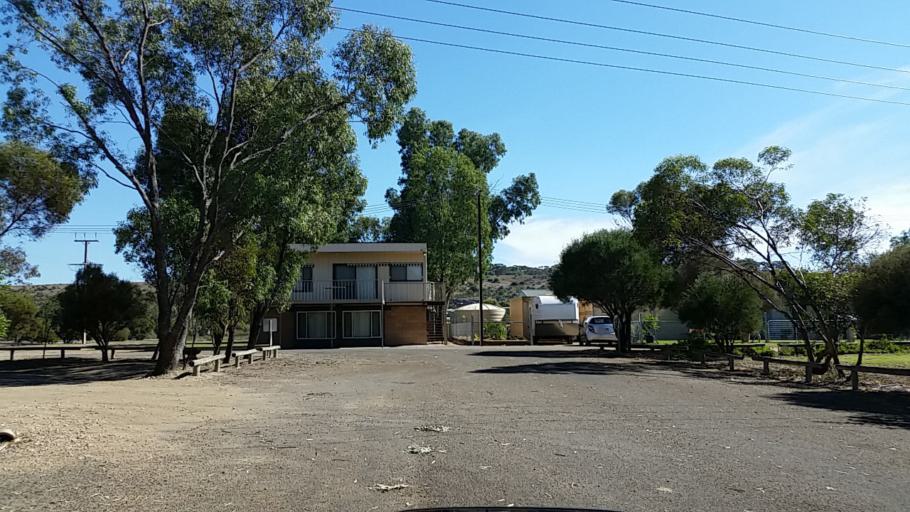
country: AU
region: South Australia
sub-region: Mid Murray
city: Mannum
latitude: -34.7078
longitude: 139.5722
